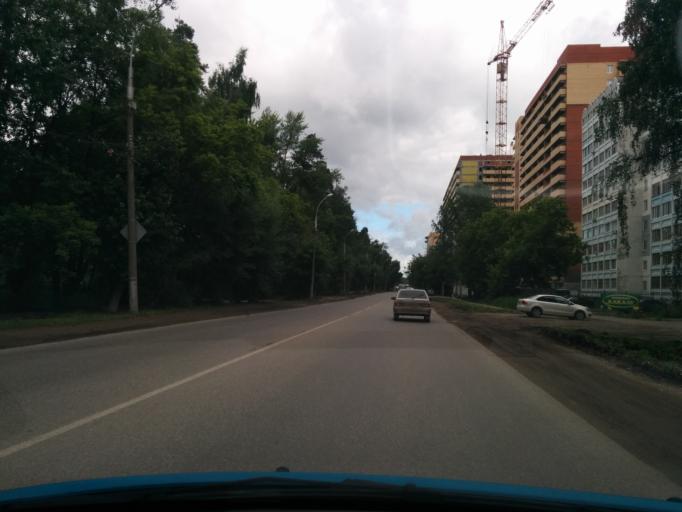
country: RU
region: Perm
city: Kondratovo
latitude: 58.0289
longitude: 56.0174
